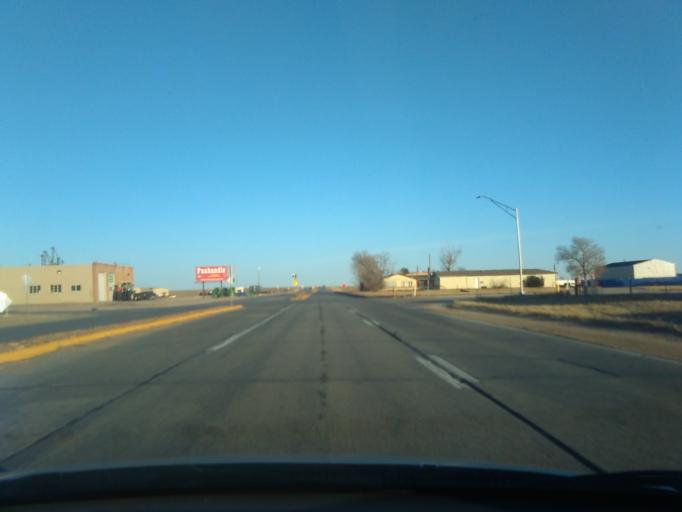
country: US
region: Nebraska
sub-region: Cheyenne County
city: Sidney
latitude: 41.1447
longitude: -102.9551
